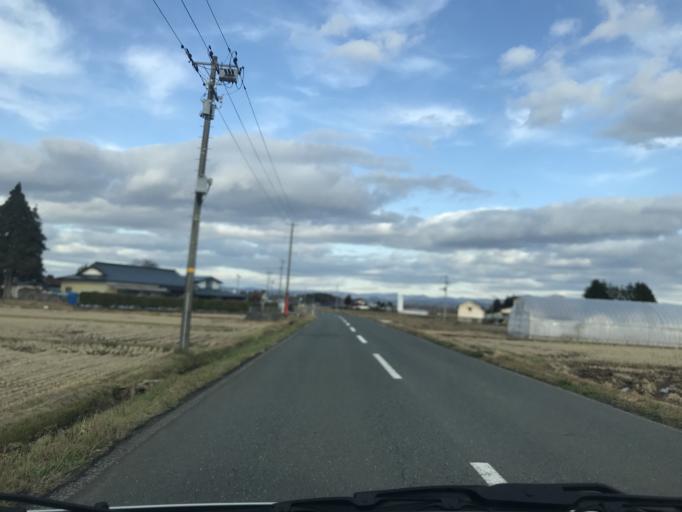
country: JP
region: Iwate
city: Mizusawa
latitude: 39.1759
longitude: 141.0958
